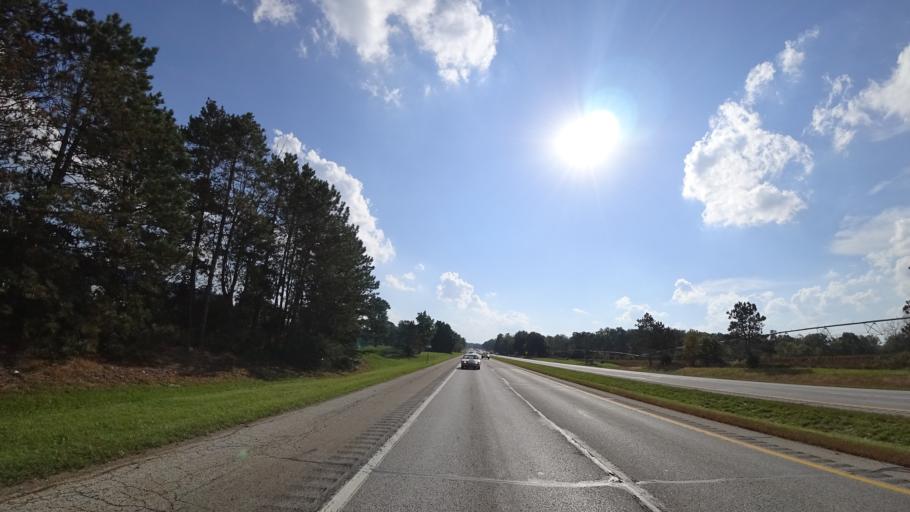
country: US
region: Michigan
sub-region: Saint Joseph County
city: Three Rivers
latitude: 41.9579
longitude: -85.6441
